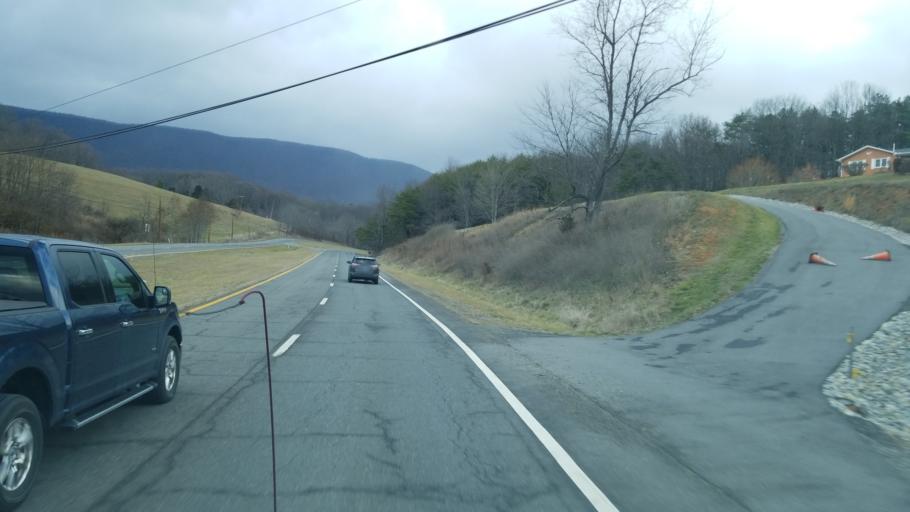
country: US
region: Virginia
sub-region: Giles County
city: Pearisburg
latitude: 37.2810
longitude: -80.7422
